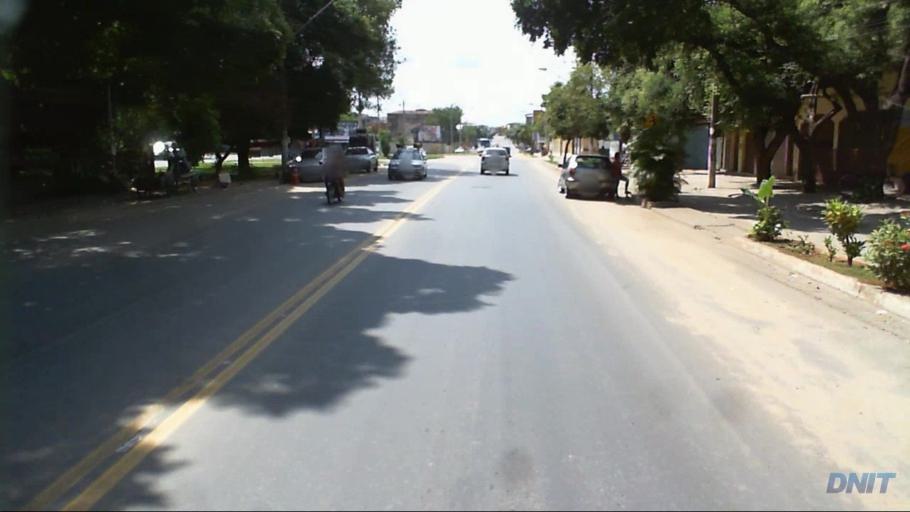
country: BR
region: Minas Gerais
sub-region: Governador Valadares
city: Governador Valadares
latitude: -18.8858
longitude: -41.9696
